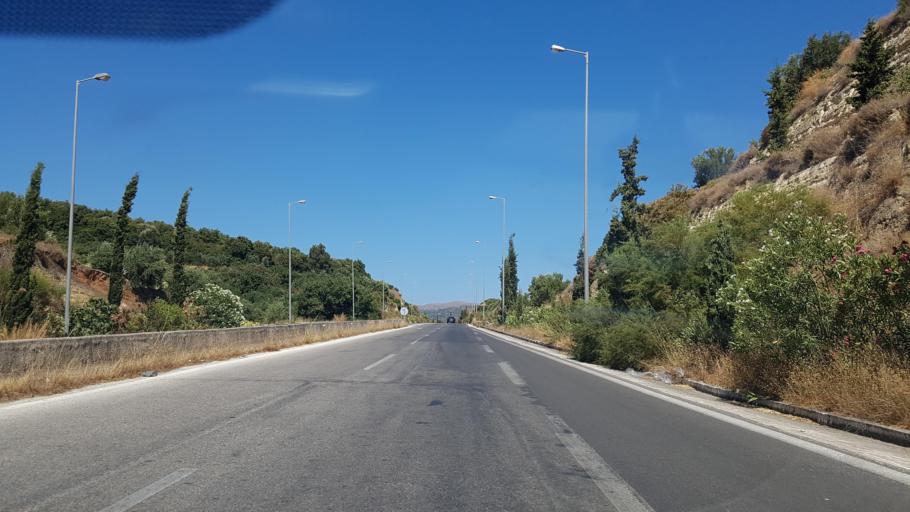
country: GR
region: Crete
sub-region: Nomos Chanias
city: Kolympari
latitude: 35.5213
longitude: 23.8157
